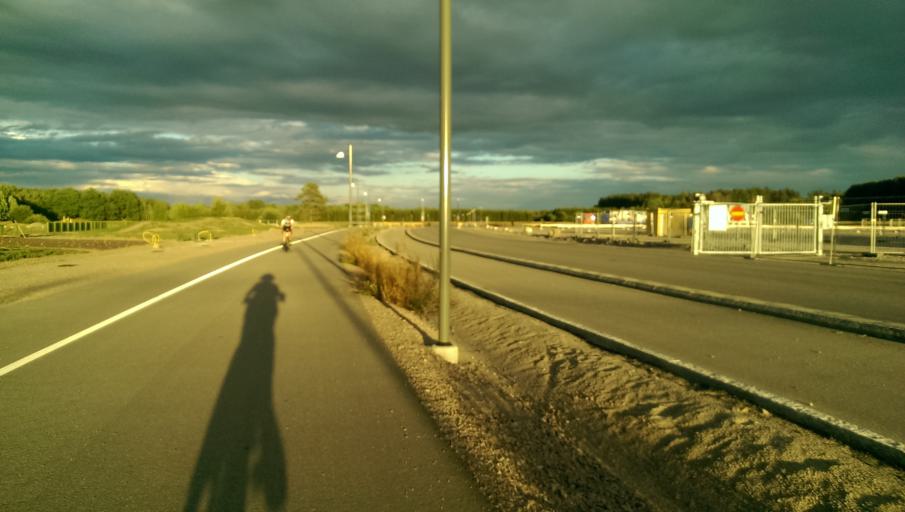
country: SE
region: OEstergoetland
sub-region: Linkopings Kommun
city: Linkoping
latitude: 58.3935
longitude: 15.5863
